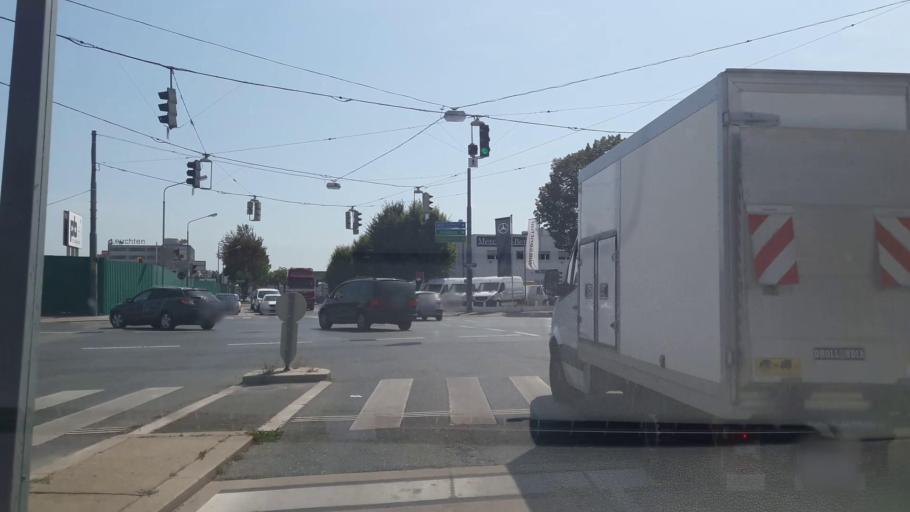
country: AT
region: Lower Austria
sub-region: Politischer Bezirk Modling
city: Vosendorf
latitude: 48.1480
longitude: 16.3609
